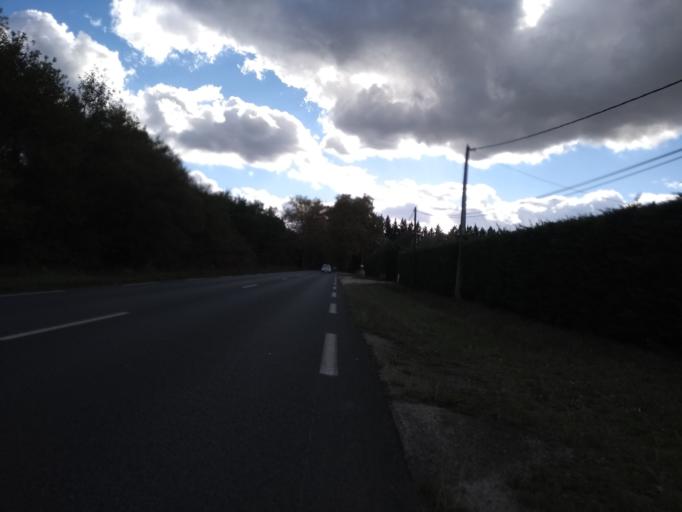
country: FR
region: Aquitaine
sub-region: Departement de la Gironde
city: Cestas
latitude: 44.7110
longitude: -0.6962
